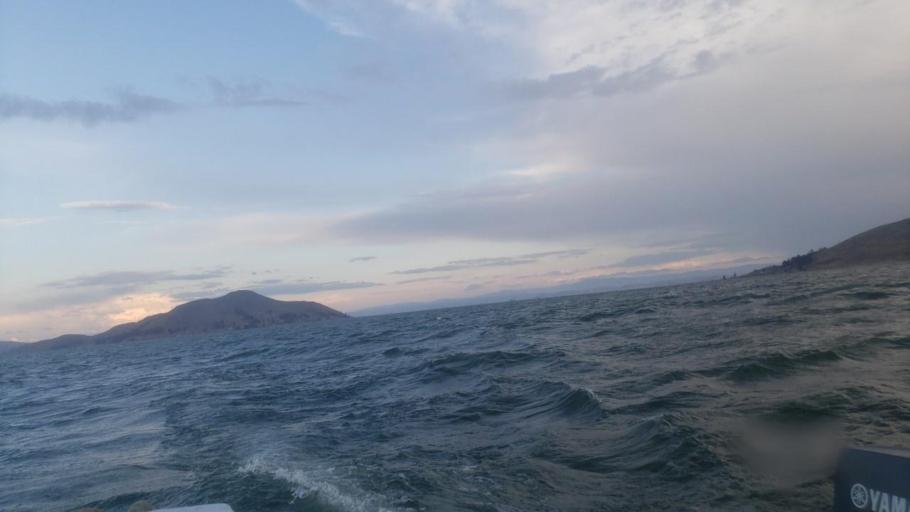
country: BO
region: La Paz
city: San Pedro
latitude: -16.2635
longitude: -68.8035
